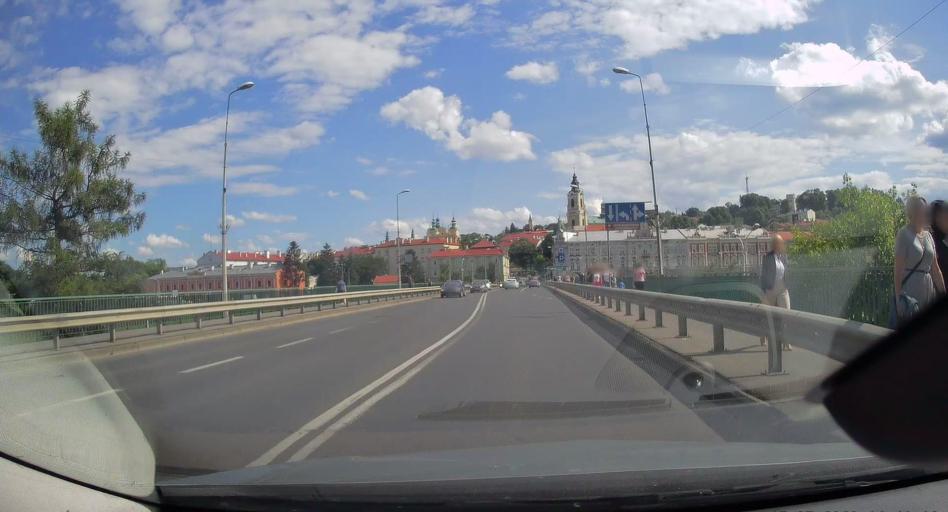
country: PL
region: Subcarpathian Voivodeship
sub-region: Przemysl
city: Przemysl
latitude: 49.7853
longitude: 22.7668
